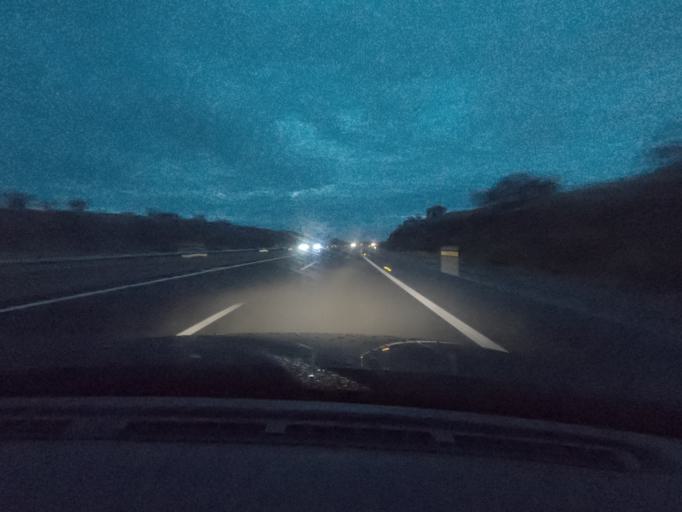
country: ES
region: Extremadura
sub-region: Provincia de Caceres
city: Caceres
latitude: 39.4056
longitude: -6.3988
